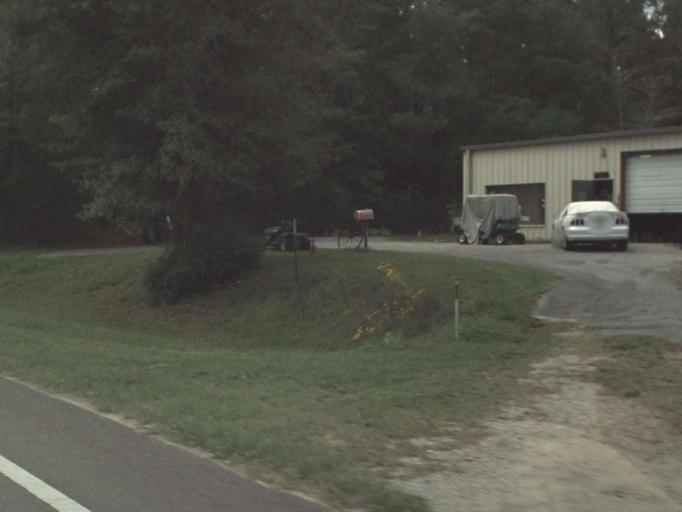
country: US
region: Florida
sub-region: Walton County
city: DeFuniak Springs
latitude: 30.6930
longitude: -85.9364
